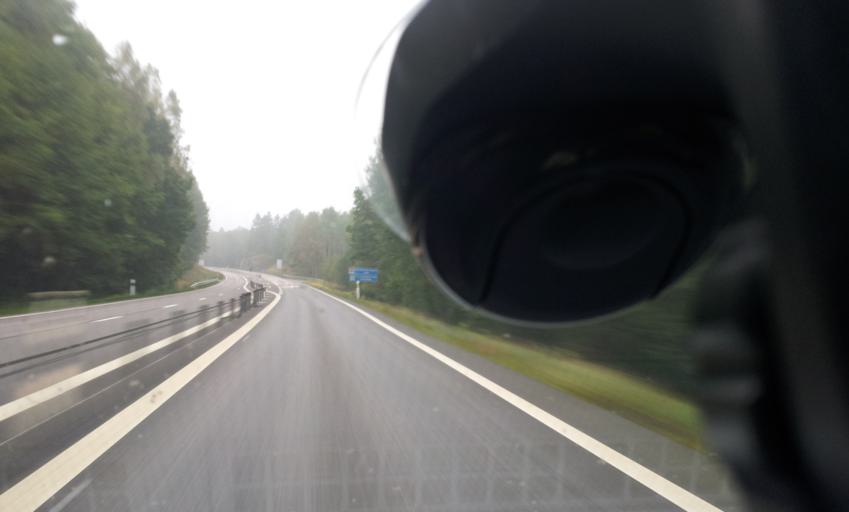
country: SE
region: OEstergoetland
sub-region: Valdemarsviks Kommun
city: Valdemarsvik
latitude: 58.1092
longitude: 16.5428
